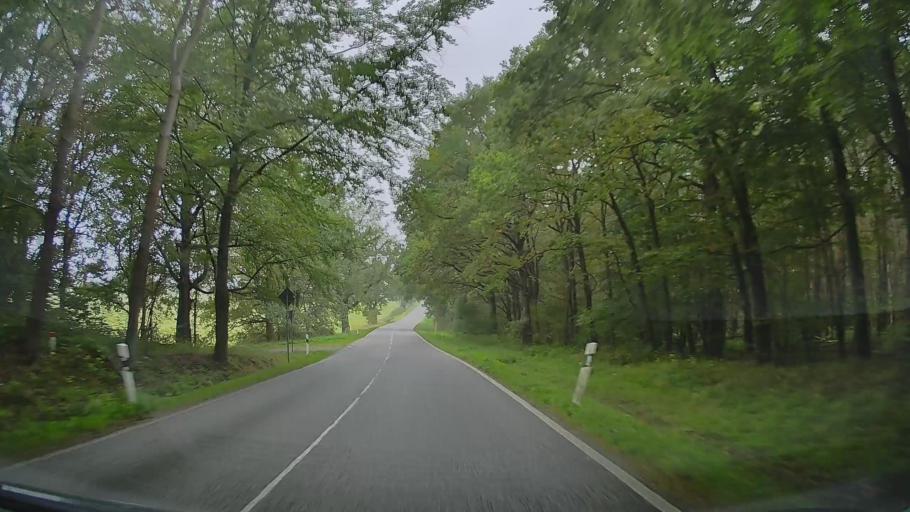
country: DE
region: Mecklenburg-Vorpommern
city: Blowatz
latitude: 53.9551
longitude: 11.5710
